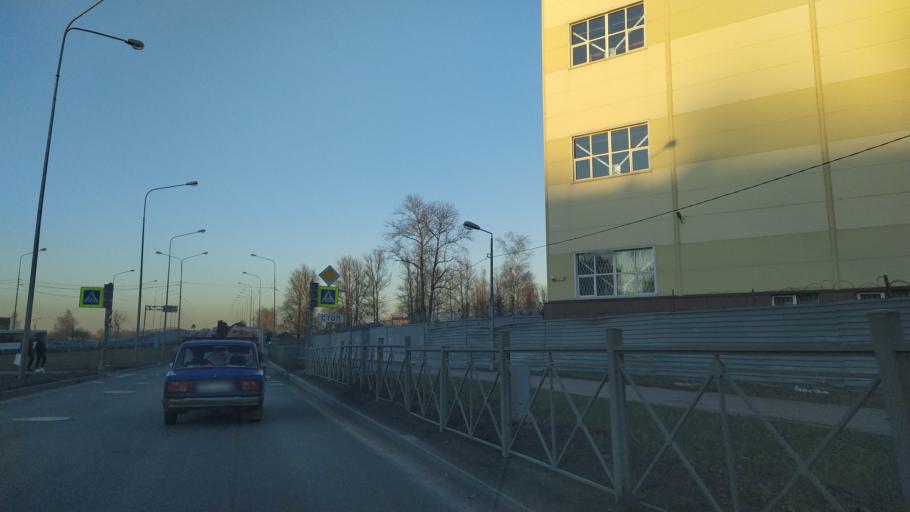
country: RU
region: St.-Petersburg
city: Krasnogvargeisky
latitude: 59.9968
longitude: 30.4390
